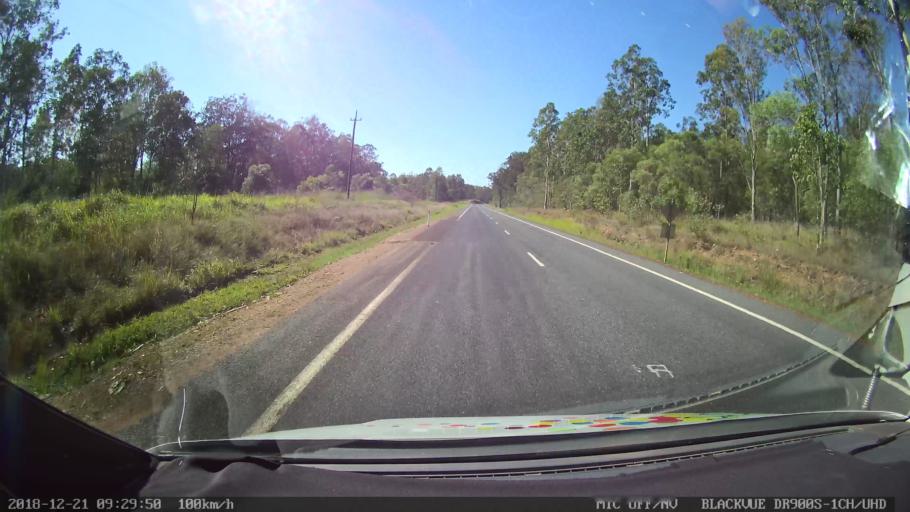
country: AU
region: New South Wales
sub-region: Clarence Valley
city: Maclean
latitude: -29.4375
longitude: 152.9905
